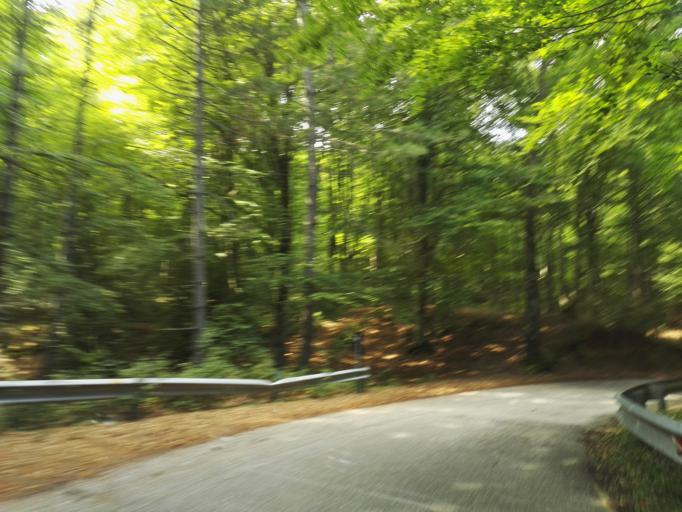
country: IT
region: Calabria
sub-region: Provincia di Vibo-Valentia
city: Nardodipace
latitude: 38.4939
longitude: 16.3783
